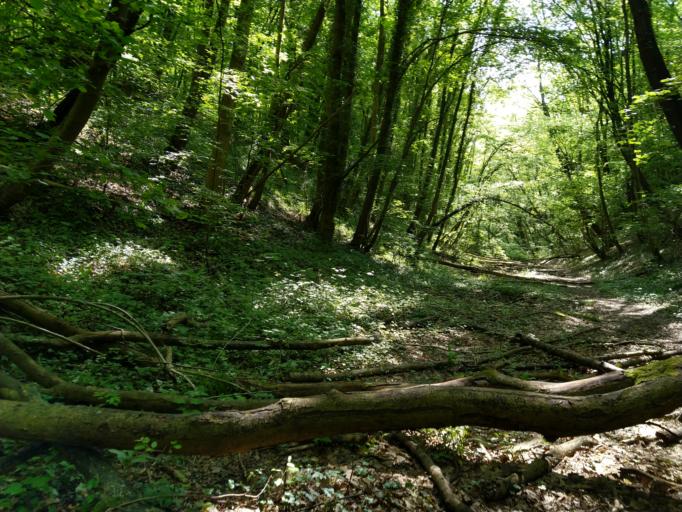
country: FR
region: Nord-Pas-de-Calais
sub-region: Departement du Nord
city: Wargnies-le-Grand
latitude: 50.3434
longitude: 3.7167
